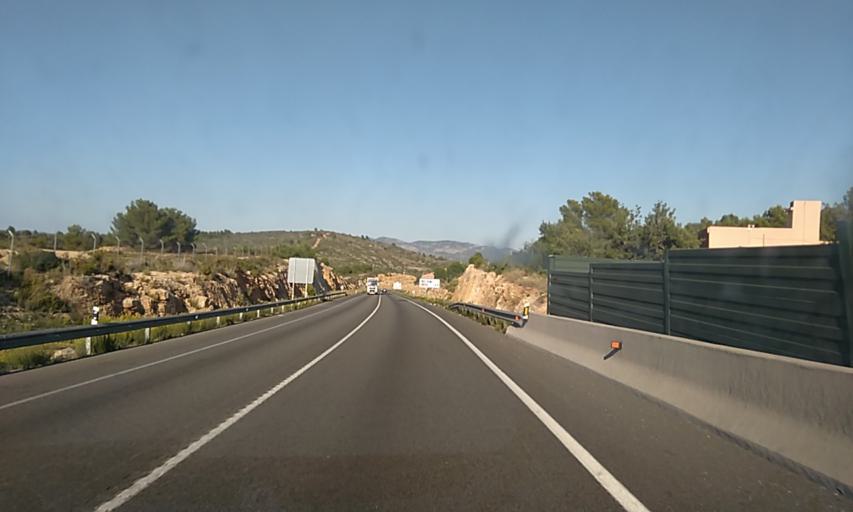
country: ES
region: Valencia
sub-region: Provincia de Castello
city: Torreblanca
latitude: 40.2236
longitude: 0.1754
